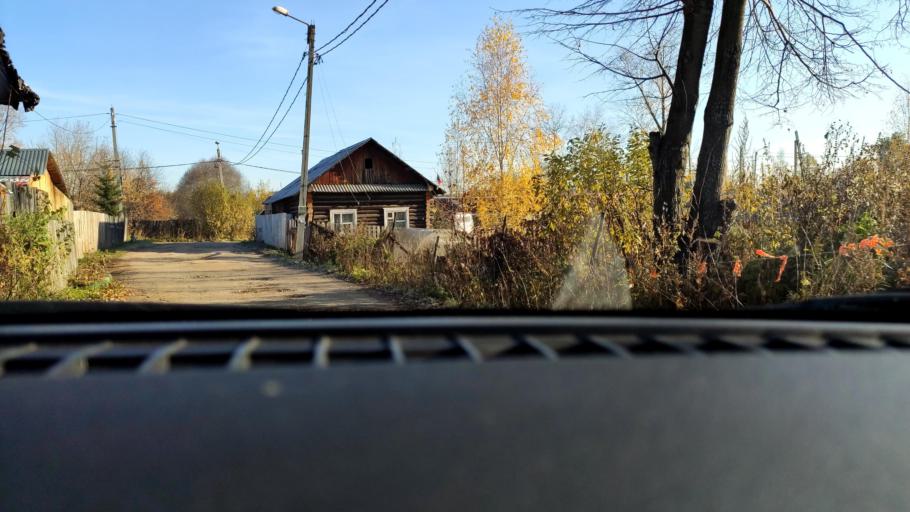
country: RU
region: Perm
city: Perm
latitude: 58.0284
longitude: 56.2110
